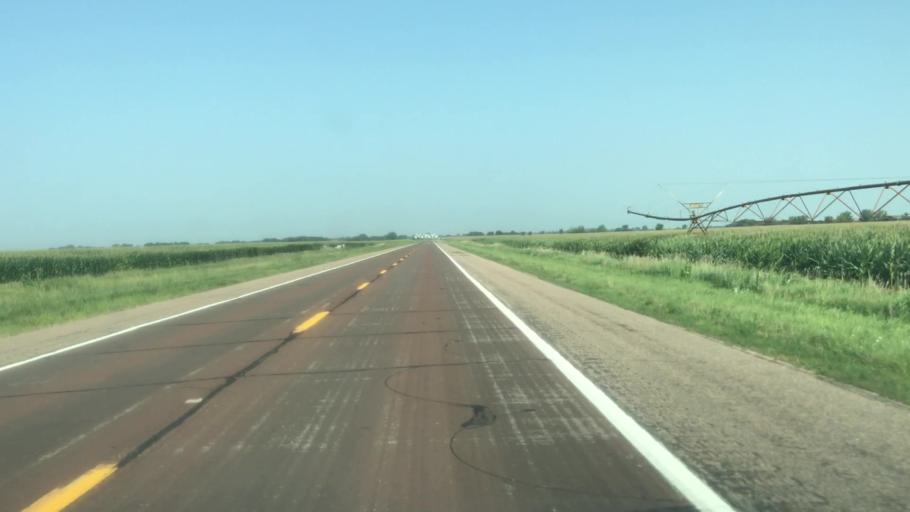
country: US
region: Nebraska
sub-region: Hall County
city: Wood River
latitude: 40.9778
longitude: -98.5168
